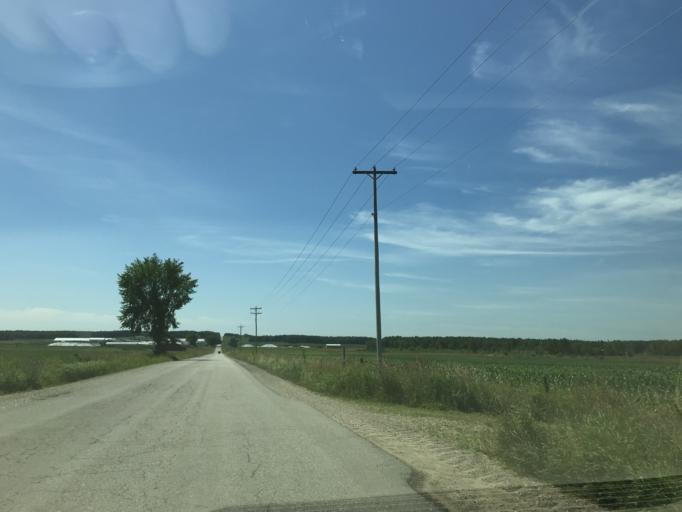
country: US
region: Michigan
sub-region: Missaukee County
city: Lake City
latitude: 44.3222
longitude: -85.0749
